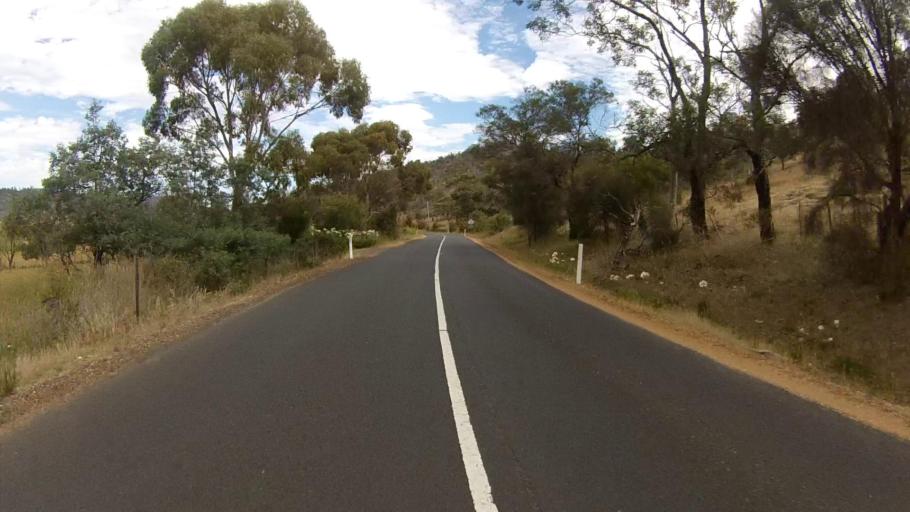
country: AU
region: Tasmania
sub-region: Clarence
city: Cambridge
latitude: -42.7399
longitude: 147.4202
